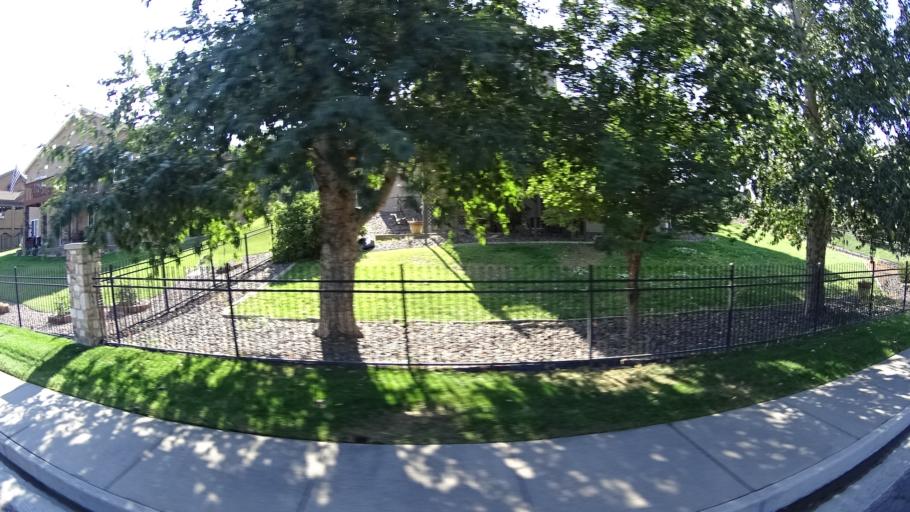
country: US
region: Colorado
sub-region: El Paso County
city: Colorado Springs
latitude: 38.8836
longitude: -104.7874
